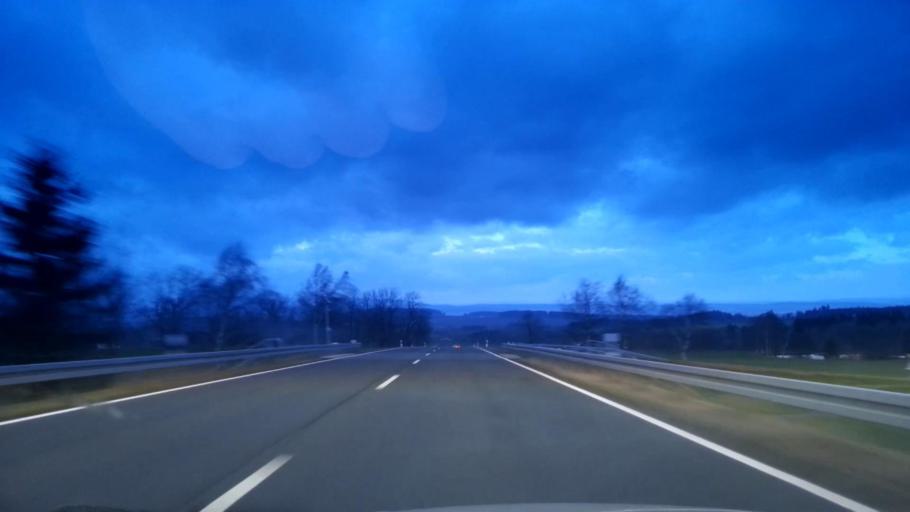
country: DE
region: Bavaria
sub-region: Upper Palatinate
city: Fuchsmuhl
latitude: 49.9426
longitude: 12.1161
